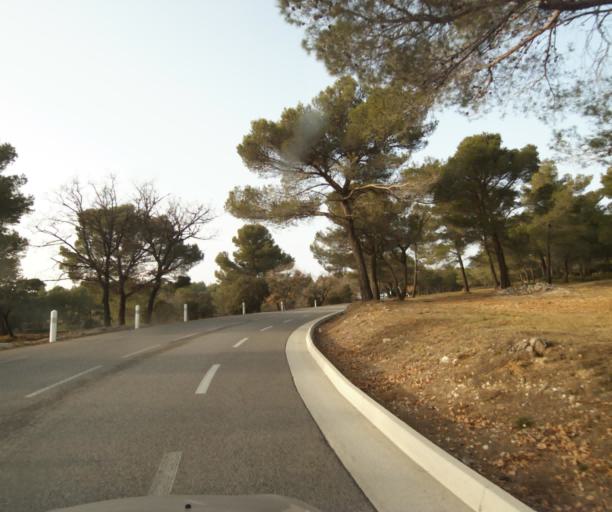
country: FR
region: Provence-Alpes-Cote d'Azur
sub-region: Departement des Bouches-du-Rhone
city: Rognes
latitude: 43.6244
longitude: 5.3495
